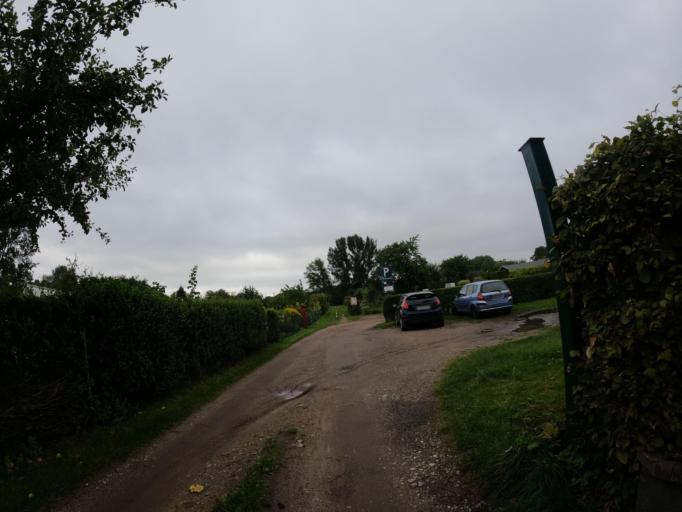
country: DE
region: Mecklenburg-Vorpommern
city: Putbus
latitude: 54.3563
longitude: 13.4663
